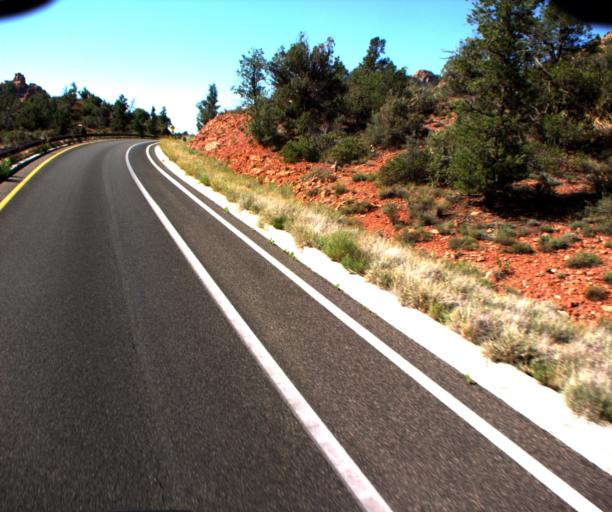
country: US
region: Arizona
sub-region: Yavapai County
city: Village of Oak Creek (Big Park)
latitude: 34.8138
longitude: -111.7689
